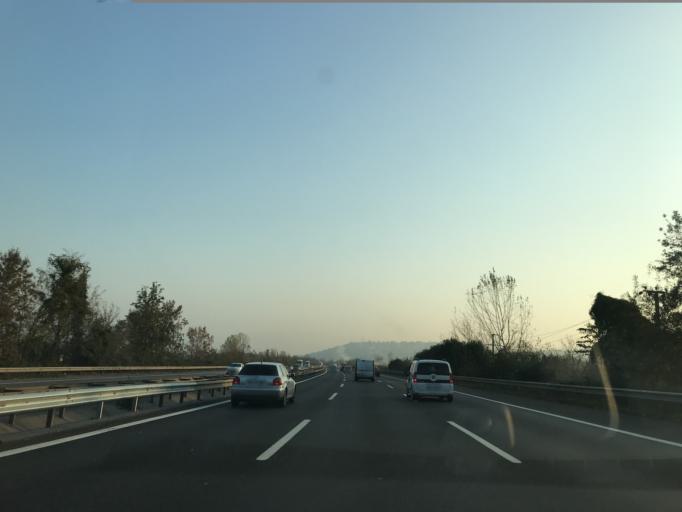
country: TR
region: Sakarya
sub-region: Merkez
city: Sapanca
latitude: 40.6819
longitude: 30.2617
